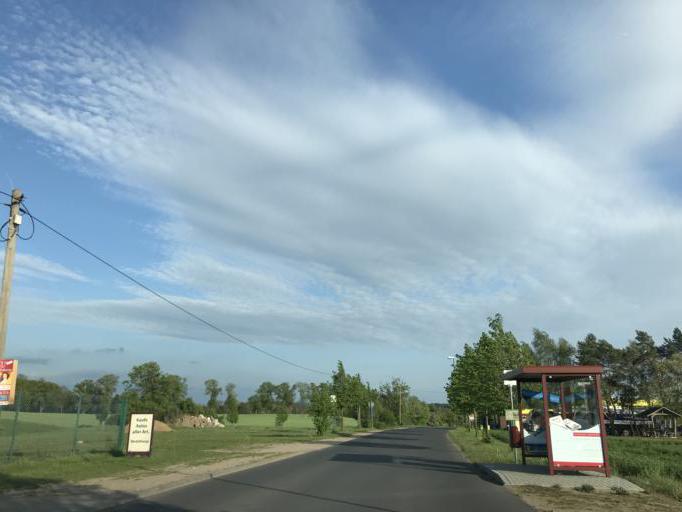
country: DE
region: Brandenburg
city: Joachimsthal
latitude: 52.9708
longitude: 13.7478
